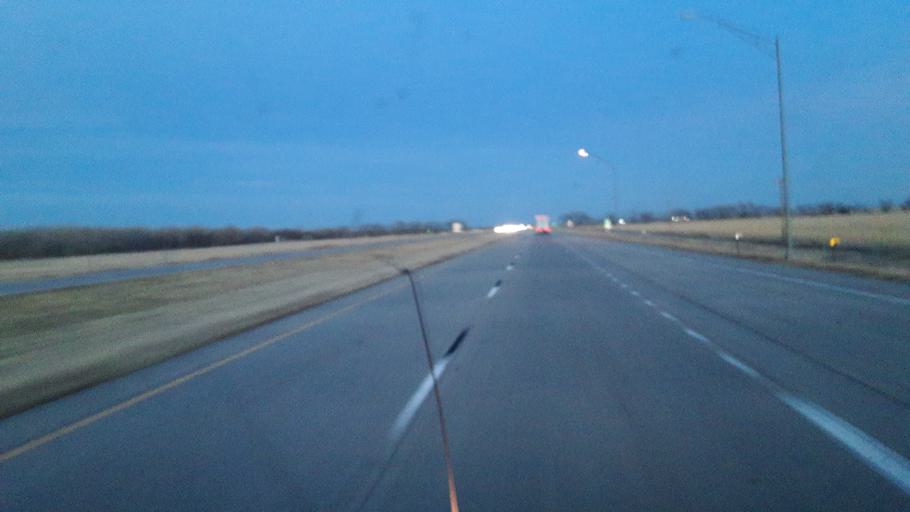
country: US
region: Nebraska
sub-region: Keith County
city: Ogallala
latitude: 41.1177
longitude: -101.5681
